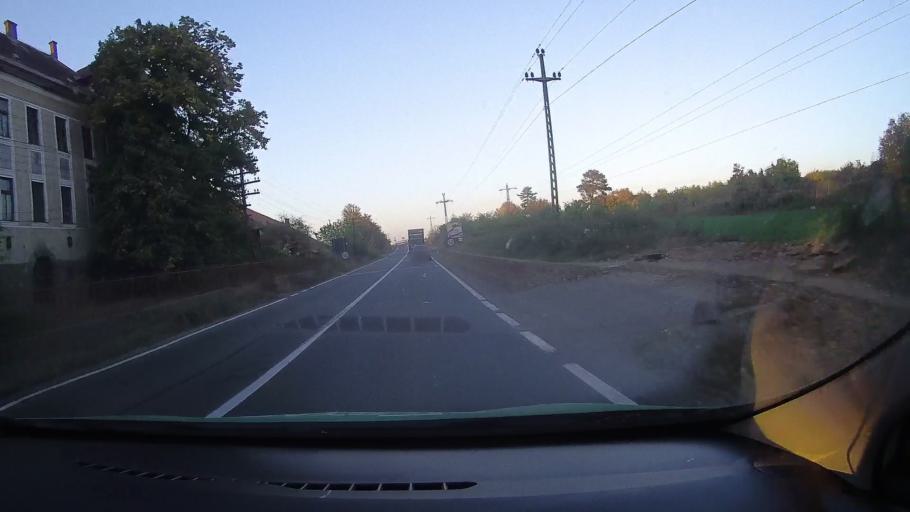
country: RO
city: Dioszeg
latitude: 47.2994
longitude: 22.0145
